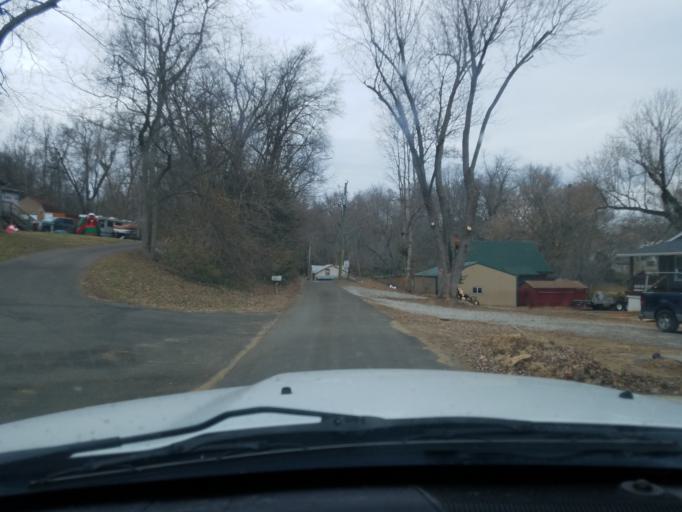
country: US
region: Kentucky
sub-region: Jefferson County
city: Prospect
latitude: 38.3370
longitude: -85.6543
